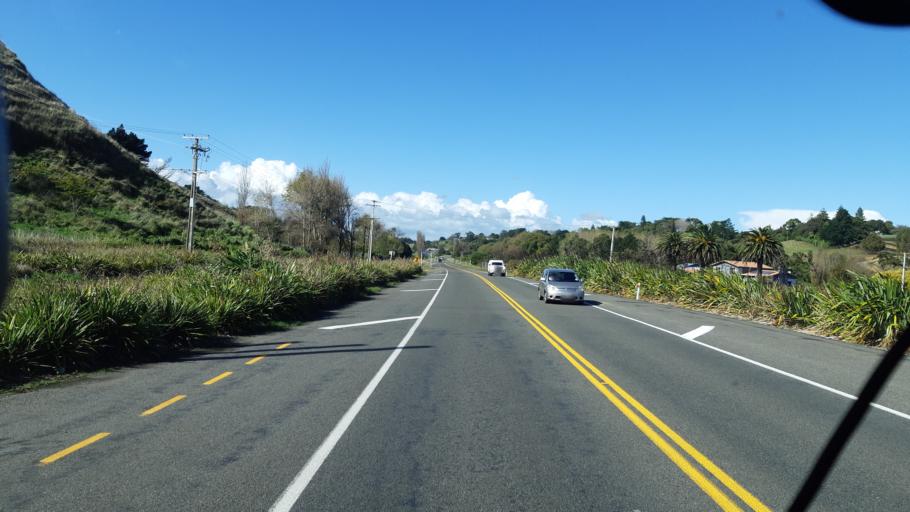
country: NZ
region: Manawatu-Wanganui
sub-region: Wanganui District
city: Wanganui
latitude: -39.9503
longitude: 175.0545
